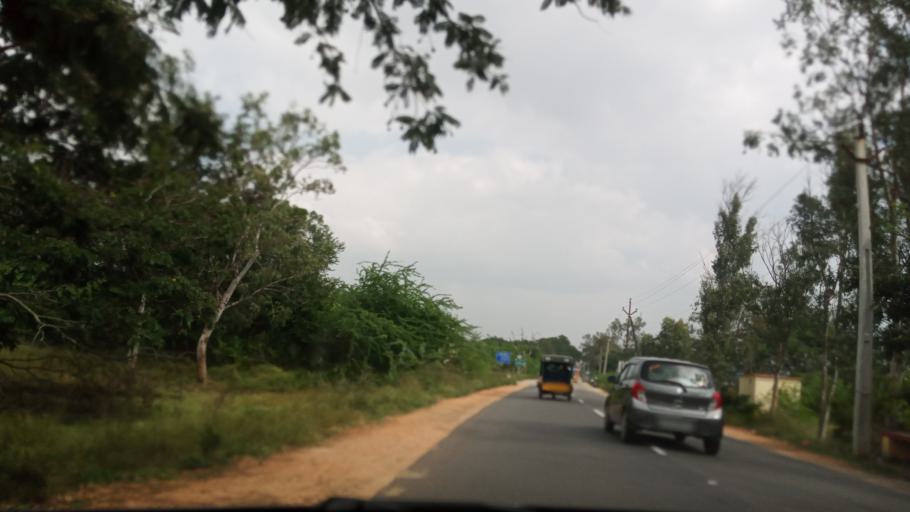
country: IN
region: Andhra Pradesh
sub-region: Chittoor
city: Madanapalle
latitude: 13.6344
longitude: 78.6217
